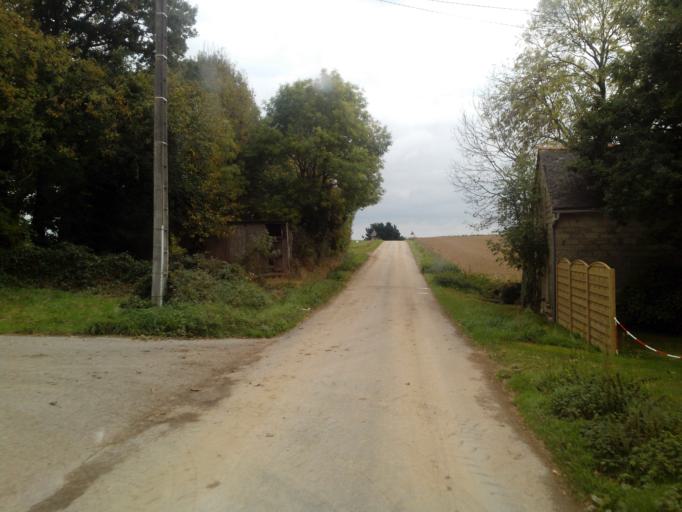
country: FR
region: Brittany
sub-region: Departement du Morbihan
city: Mauron
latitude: 48.0721
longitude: -2.3473
